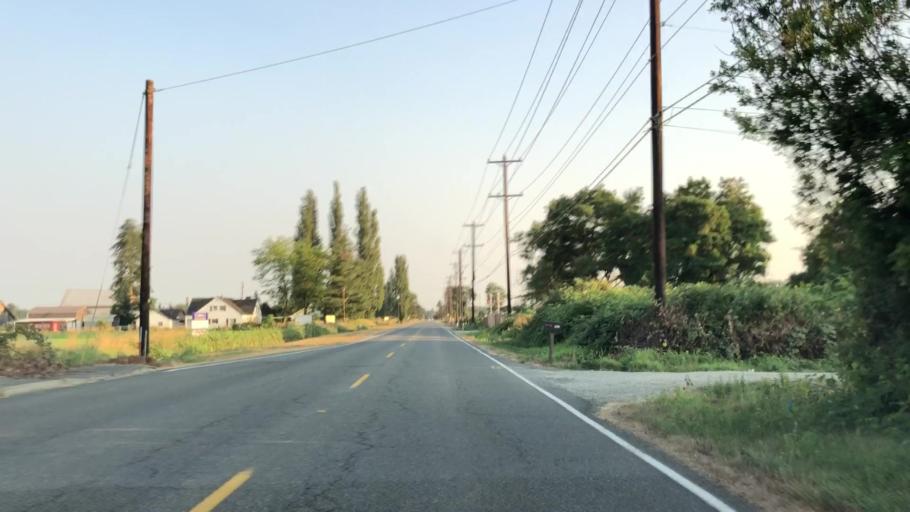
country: US
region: Washington
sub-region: Snohomish County
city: Smokey Point
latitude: 48.1468
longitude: -122.1617
